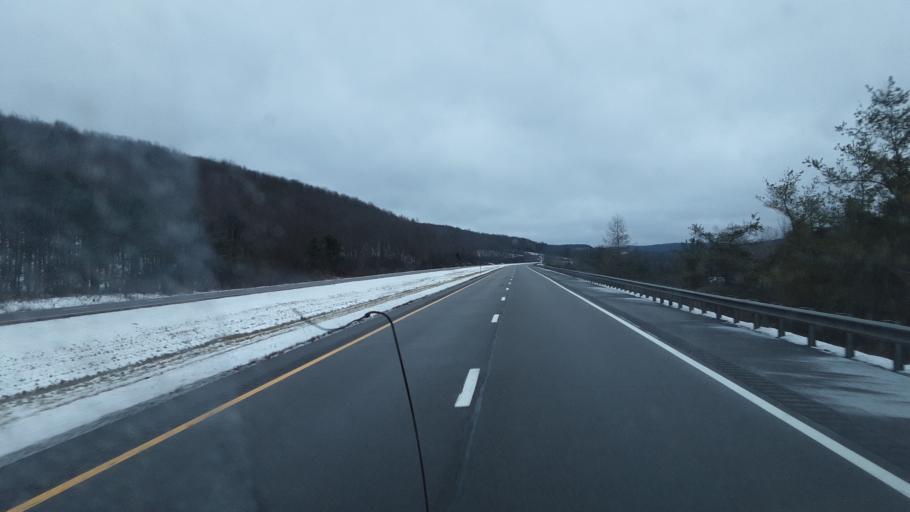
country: US
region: New York
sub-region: Allegany County
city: Alfred
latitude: 42.3171
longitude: -77.7782
